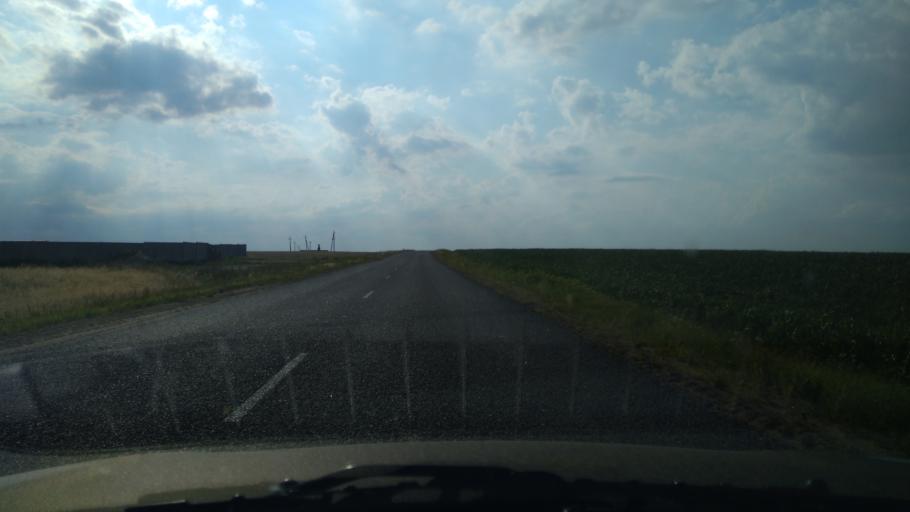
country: BY
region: Brest
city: Lyakhavichy
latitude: 53.0314
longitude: 26.3103
